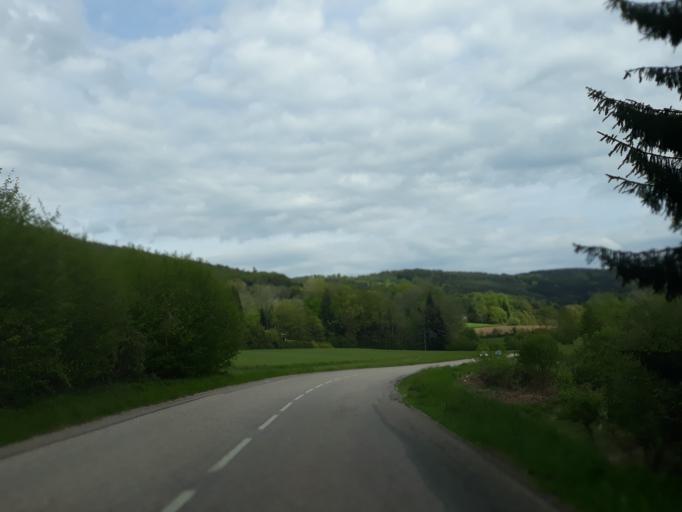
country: FR
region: Lorraine
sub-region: Departement des Vosges
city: Granges-sur-Vologne
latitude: 48.1746
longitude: 6.7690
